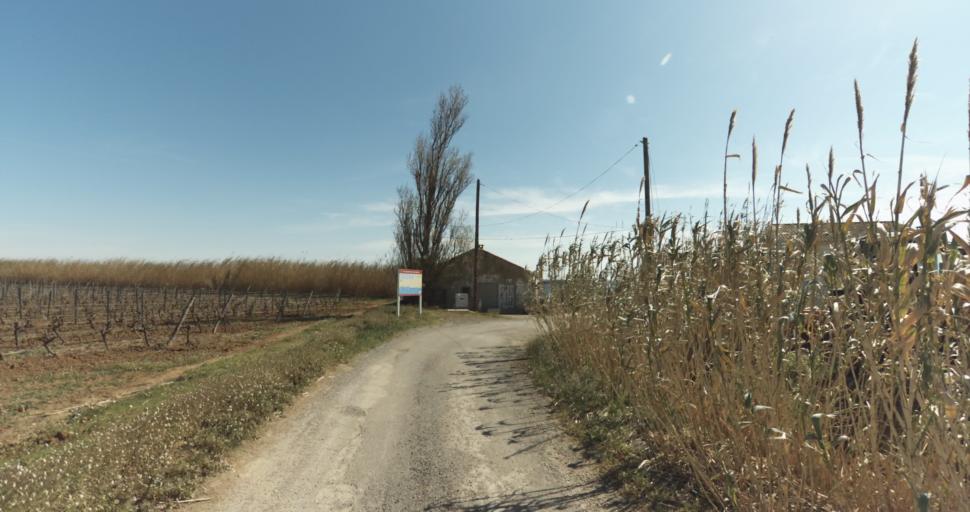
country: FR
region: Languedoc-Roussillon
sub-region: Departement de l'Herault
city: Marseillan
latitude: 43.3719
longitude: 3.5420
